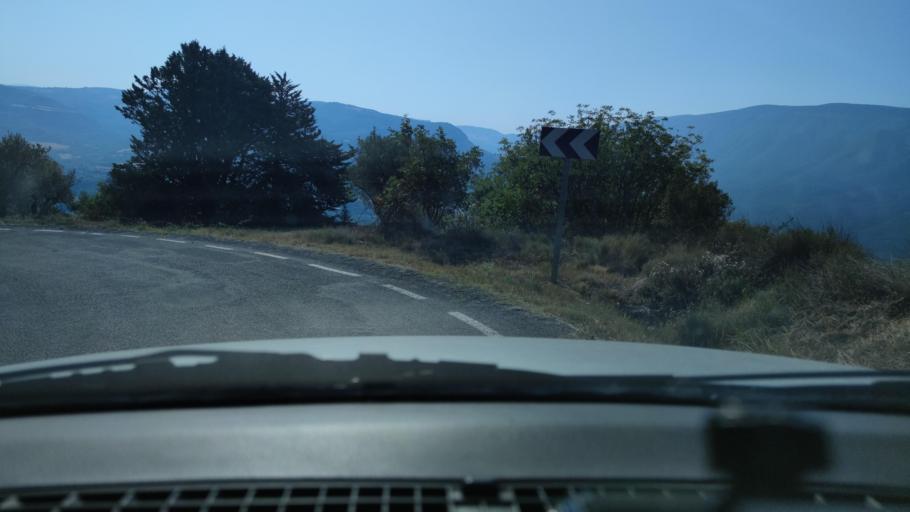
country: ES
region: Catalonia
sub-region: Provincia de Lleida
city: Llimiana
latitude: 42.0854
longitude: 0.8669
